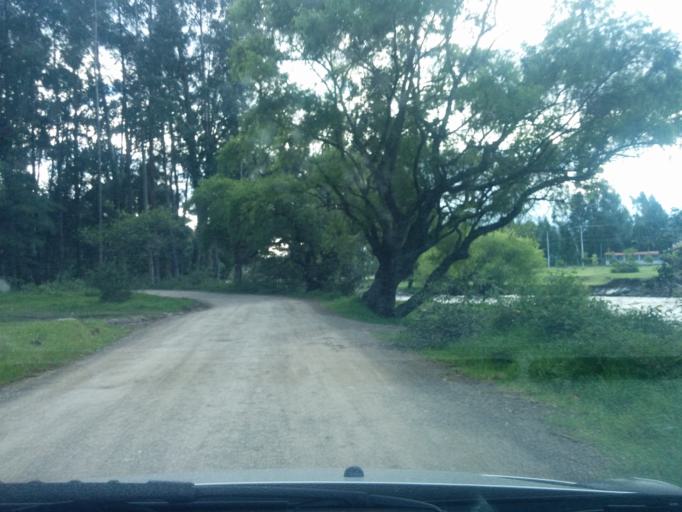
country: EC
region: Azuay
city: Cuenca
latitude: -2.8843
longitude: -78.9496
